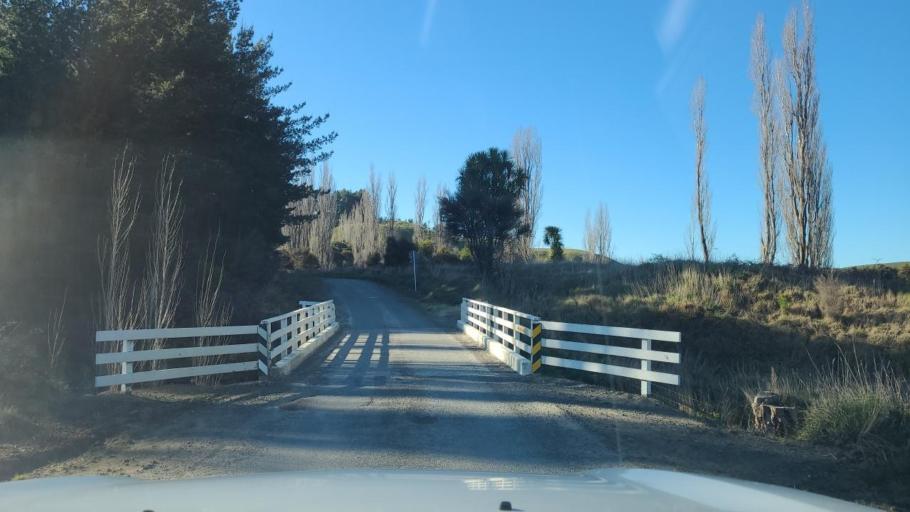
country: NZ
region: Hawke's Bay
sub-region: Napier City
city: Taradale
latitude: -39.3756
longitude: 176.5741
